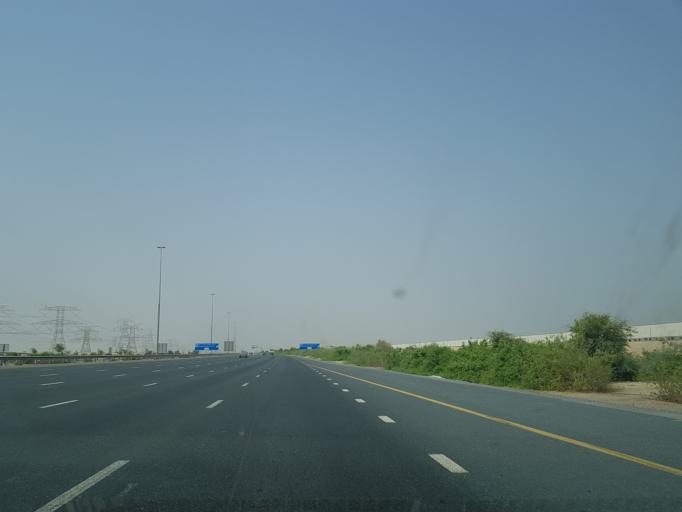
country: AE
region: Dubai
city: Dubai
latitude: 25.0570
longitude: 55.3174
